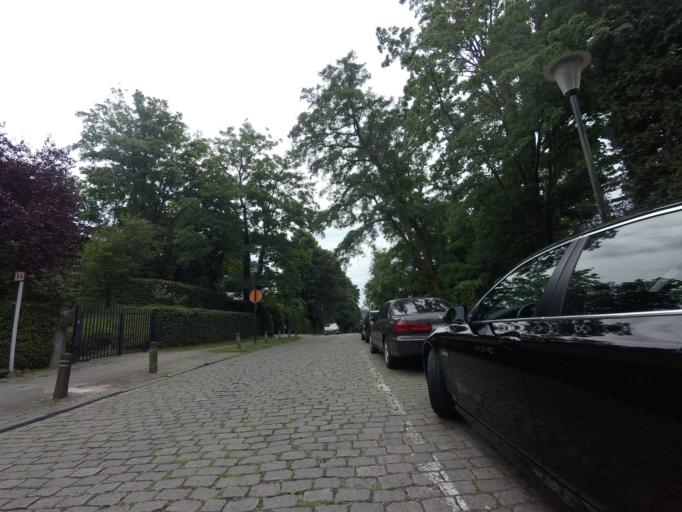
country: BE
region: Brussels Capital
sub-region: Bruxelles-Capitale
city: Brussels
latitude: 50.8088
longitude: 4.3631
